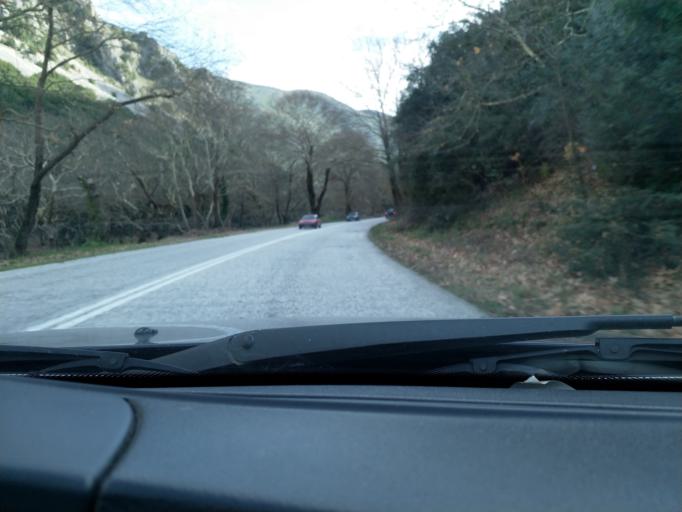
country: GR
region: Epirus
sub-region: Nomos Prevezis
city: Pappadates
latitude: 39.3973
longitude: 20.8407
